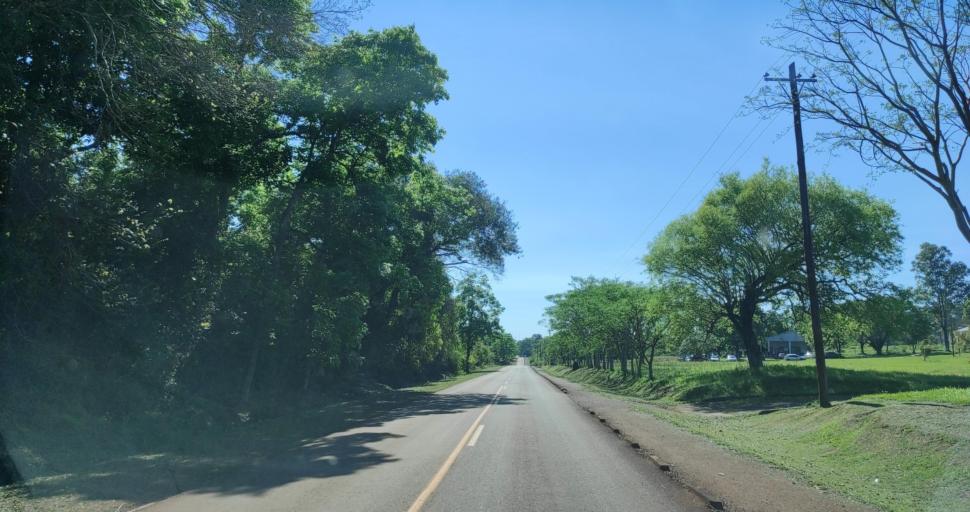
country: AR
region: Misiones
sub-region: Departamento de Candelaria
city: Loreto
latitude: -27.3370
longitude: -55.5285
